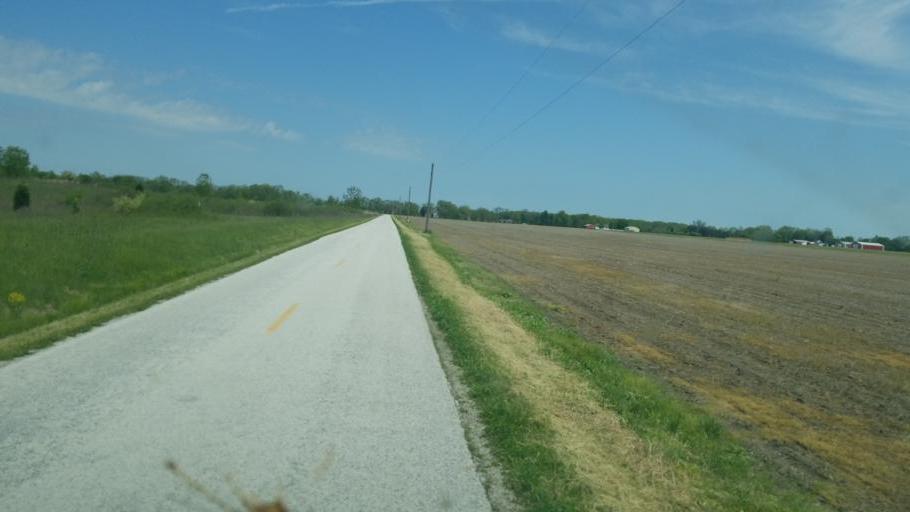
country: US
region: Ohio
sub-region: Ottawa County
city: Oak Harbor
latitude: 41.4875
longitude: -83.2020
